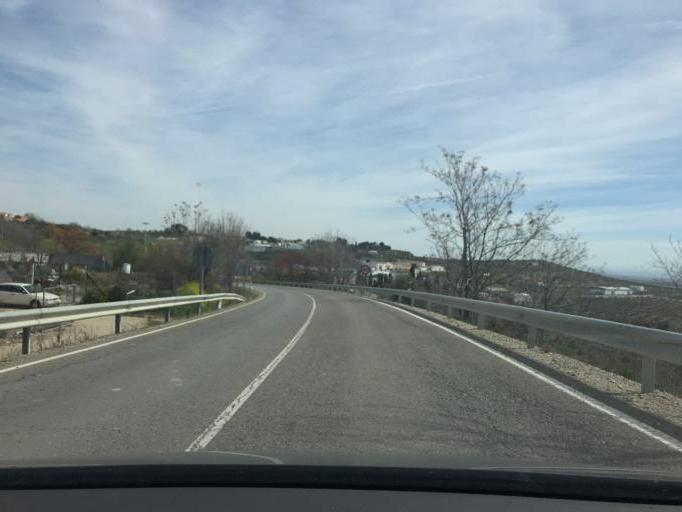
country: ES
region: Andalusia
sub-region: Provincia de Jaen
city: Porcuna
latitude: 37.8679
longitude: -4.1760
